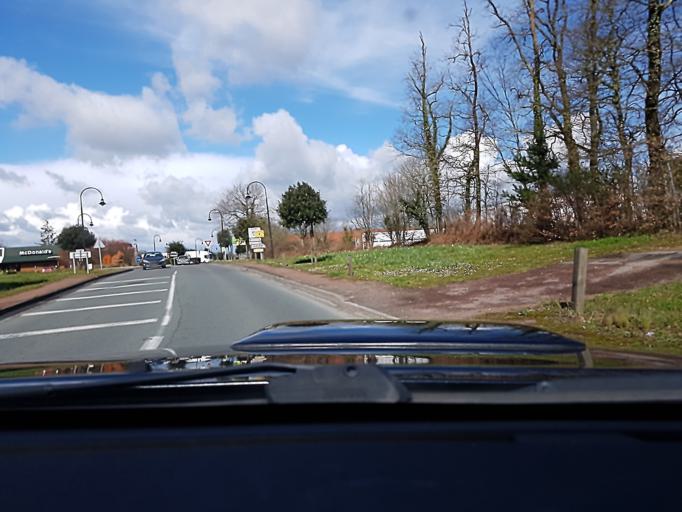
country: FR
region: Pays de la Loire
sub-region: Departement de la Vendee
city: Aizenay
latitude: 46.7329
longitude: -1.5884
